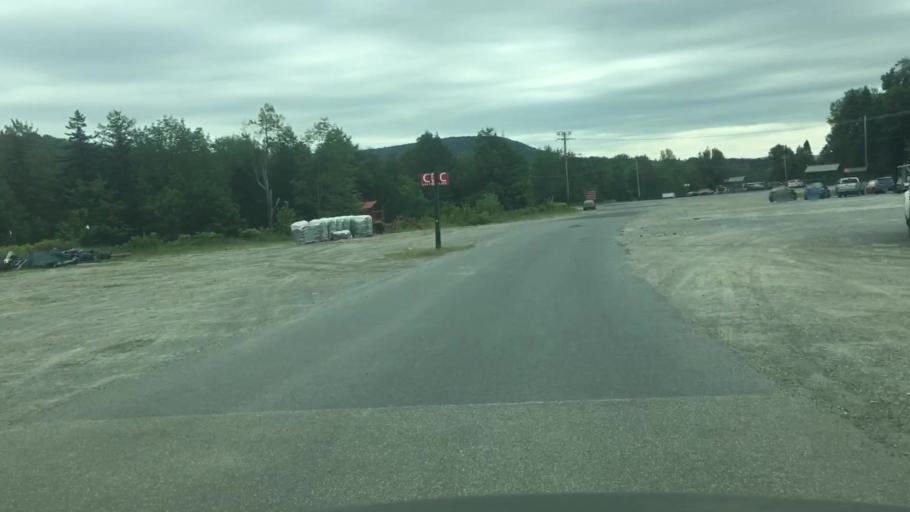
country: US
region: Vermont
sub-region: Windham County
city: Dover
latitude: 42.9702
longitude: -72.8957
